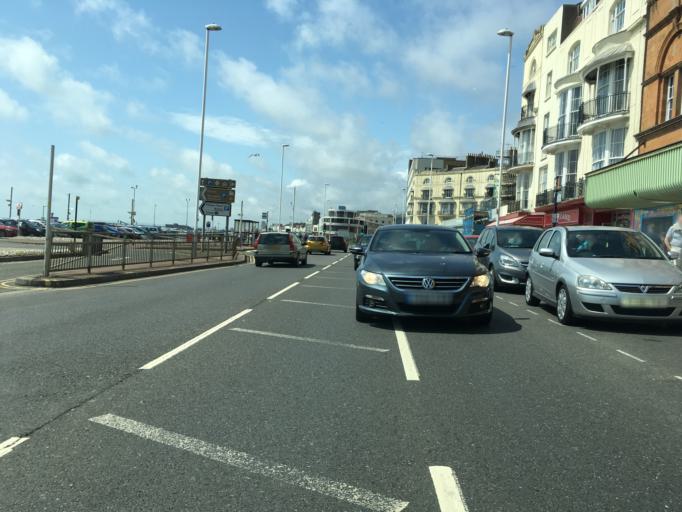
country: GB
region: England
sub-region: East Sussex
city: Hastings
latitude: 50.8553
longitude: 0.5860
